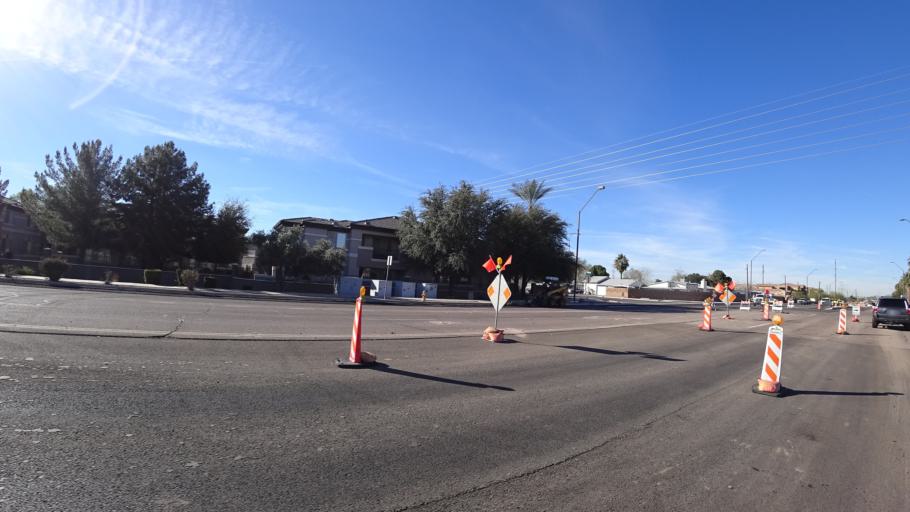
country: US
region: Arizona
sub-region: Maricopa County
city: Avondale
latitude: 33.4641
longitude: -112.3147
